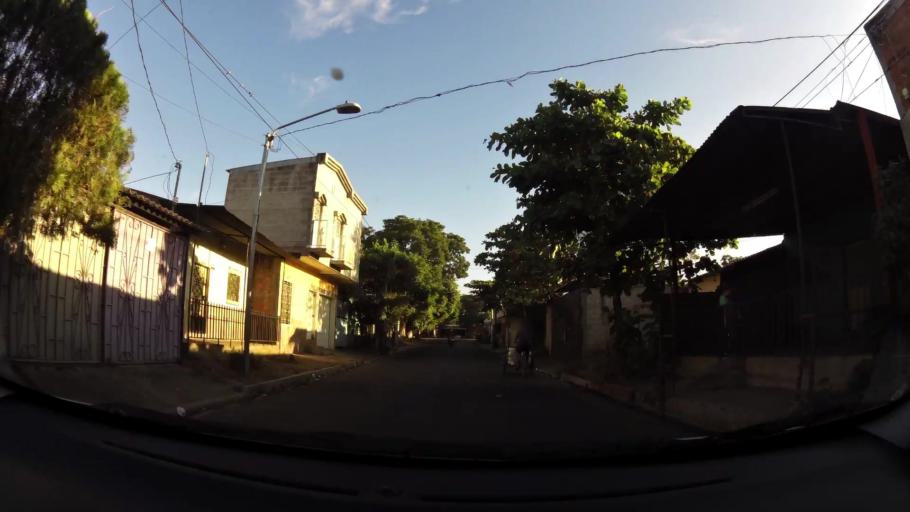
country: SV
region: Sonsonate
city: San Antonio del Monte
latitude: 13.7110
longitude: -89.7319
